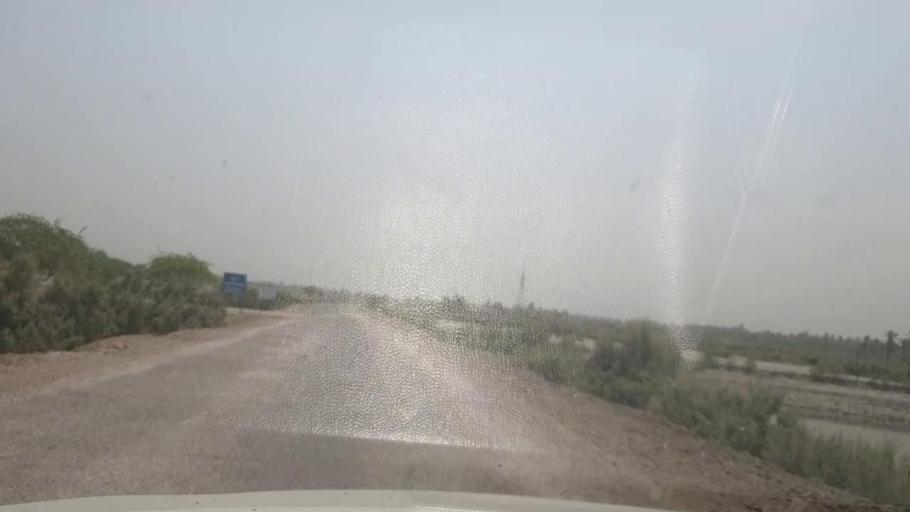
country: PK
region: Sindh
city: Kot Diji
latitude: 27.3762
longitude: 68.6995
